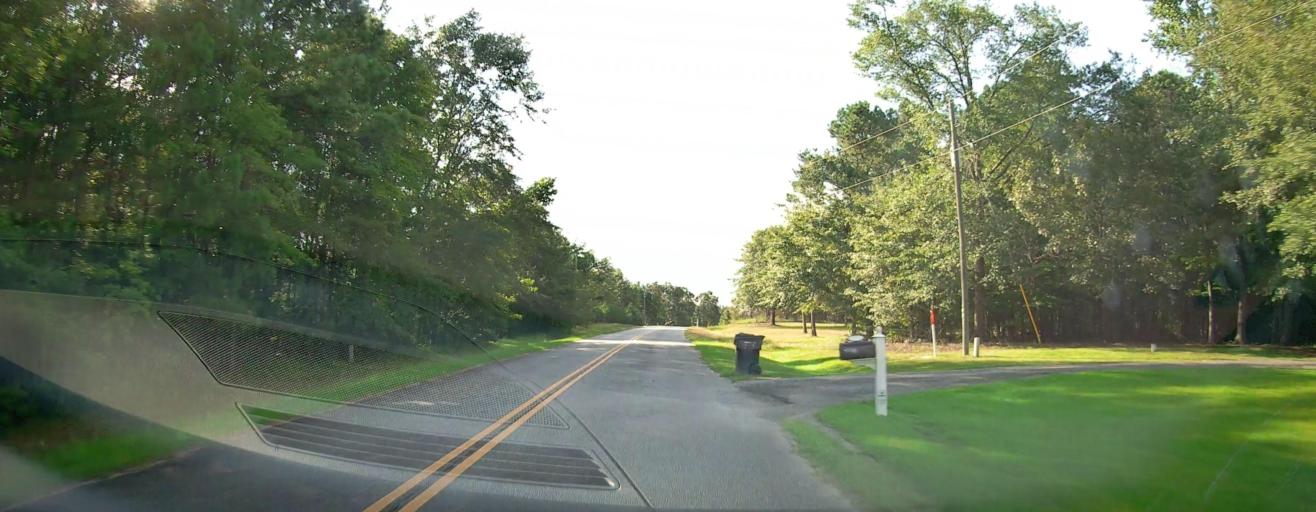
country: US
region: Georgia
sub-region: Crawford County
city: Roberta
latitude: 32.7384
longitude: -84.0132
